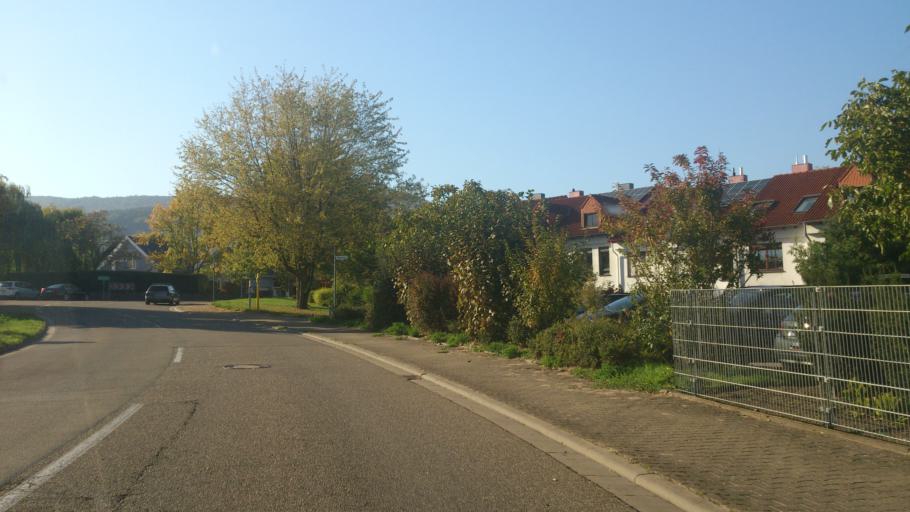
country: DE
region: Rheinland-Pfalz
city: Neustadt
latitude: 49.3405
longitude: 8.1432
